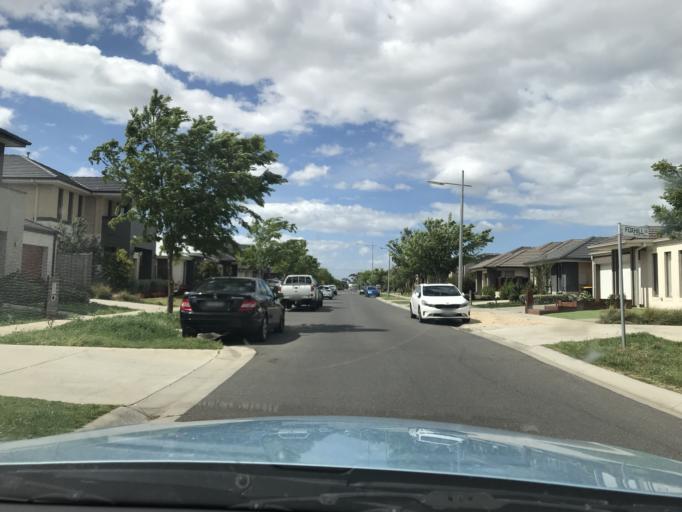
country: AU
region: Victoria
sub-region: Wyndham
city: Williams Landing
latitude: -37.8593
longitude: 144.7516
